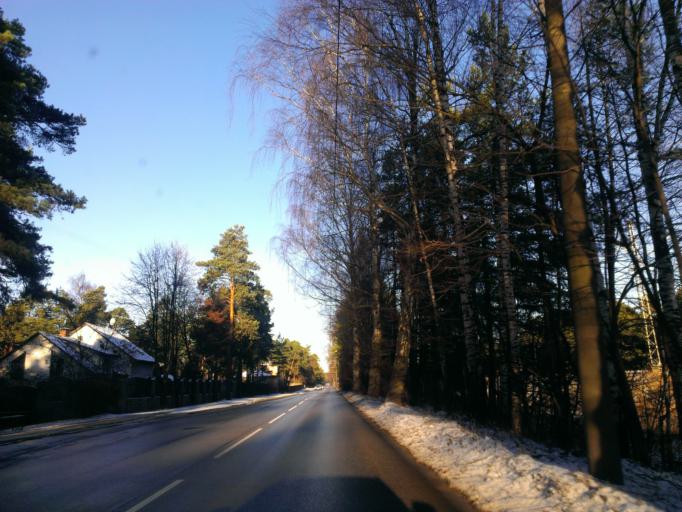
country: LV
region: Riga
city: Bolderaja
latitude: 57.0640
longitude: 24.1061
